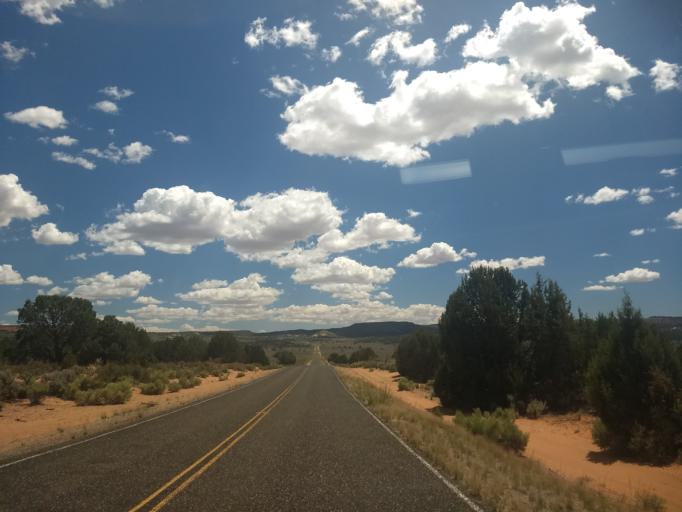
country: US
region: Utah
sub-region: Kane County
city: Kanab
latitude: 37.1719
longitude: -112.6617
